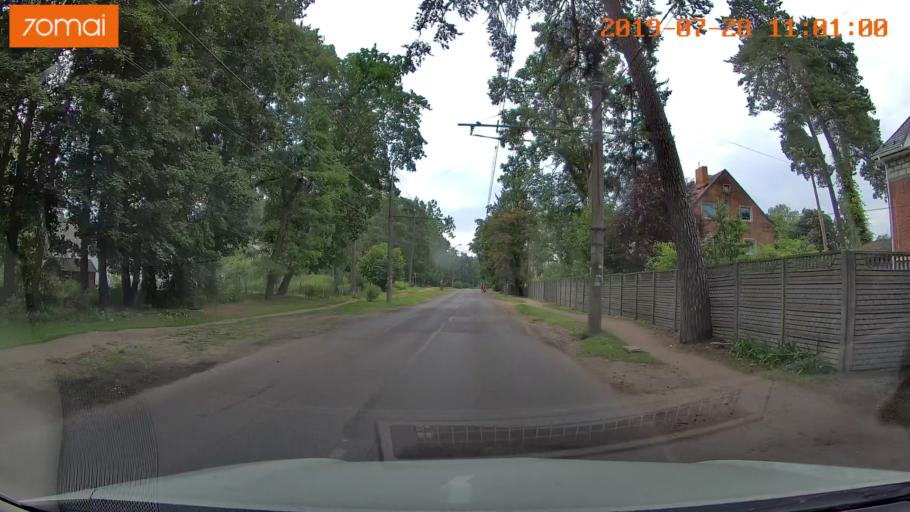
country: RU
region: Kaliningrad
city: Vzmorye
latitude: 54.7241
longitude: 20.3653
